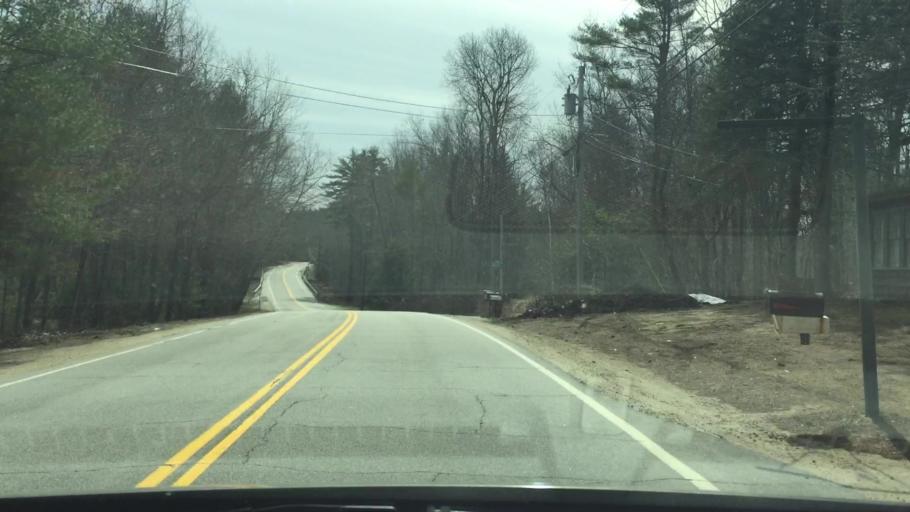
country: US
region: New Hampshire
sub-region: Strafford County
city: Barrington
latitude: 43.2421
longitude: -71.0551
